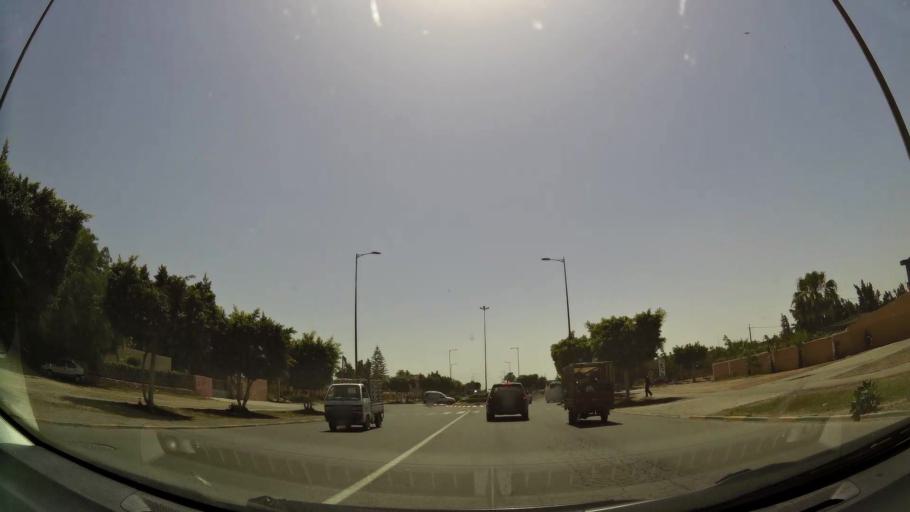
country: MA
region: Souss-Massa-Draa
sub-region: Inezgane-Ait Mellou
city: Inezgane
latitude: 30.3335
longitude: -9.4907
